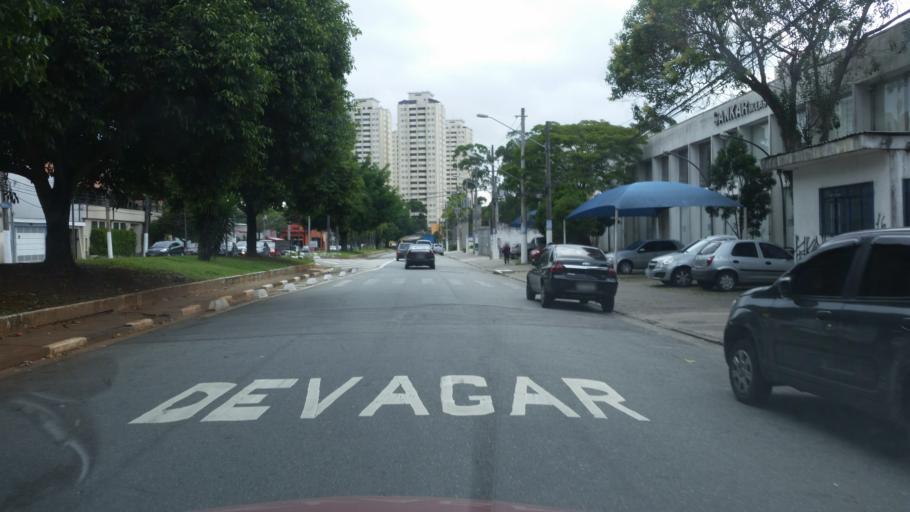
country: BR
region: Sao Paulo
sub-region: Diadema
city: Diadema
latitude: -23.6615
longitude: -46.6875
